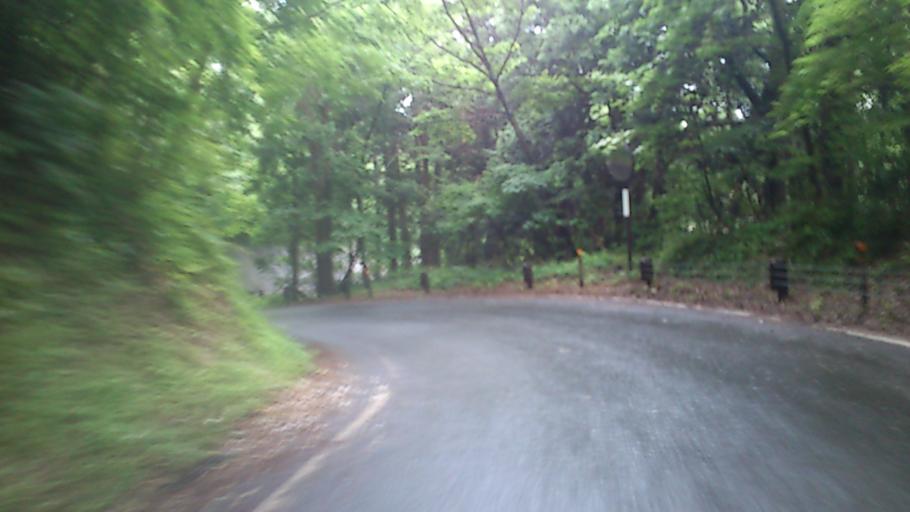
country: JP
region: Akita
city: Noshiromachi
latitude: 40.5607
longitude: 139.9625
